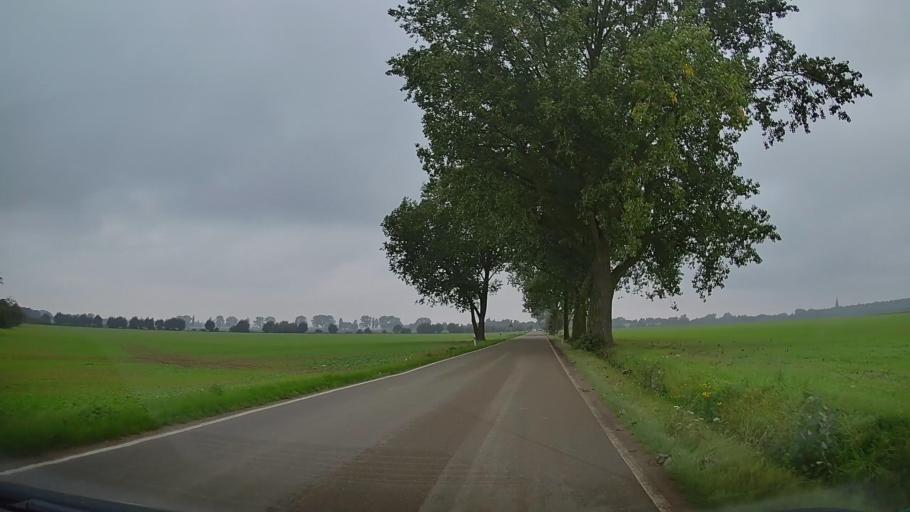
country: DE
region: Mecklenburg-Vorpommern
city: Blowatz
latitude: 53.9812
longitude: 11.5463
